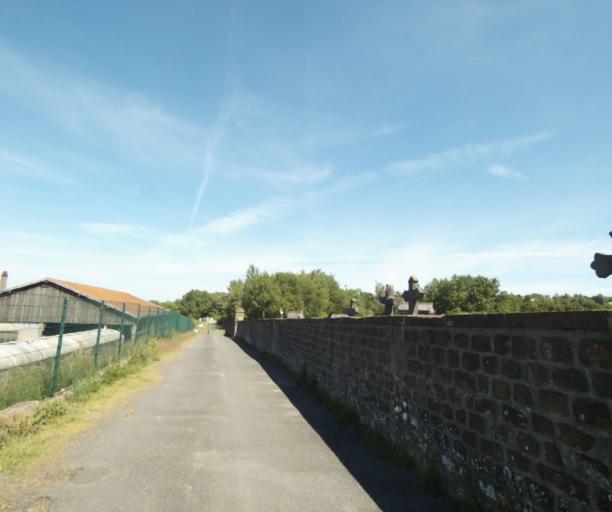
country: FR
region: Champagne-Ardenne
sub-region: Departement des Ardennes
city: Charleville-Mezieres
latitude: 49.7543
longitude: 4.7316
